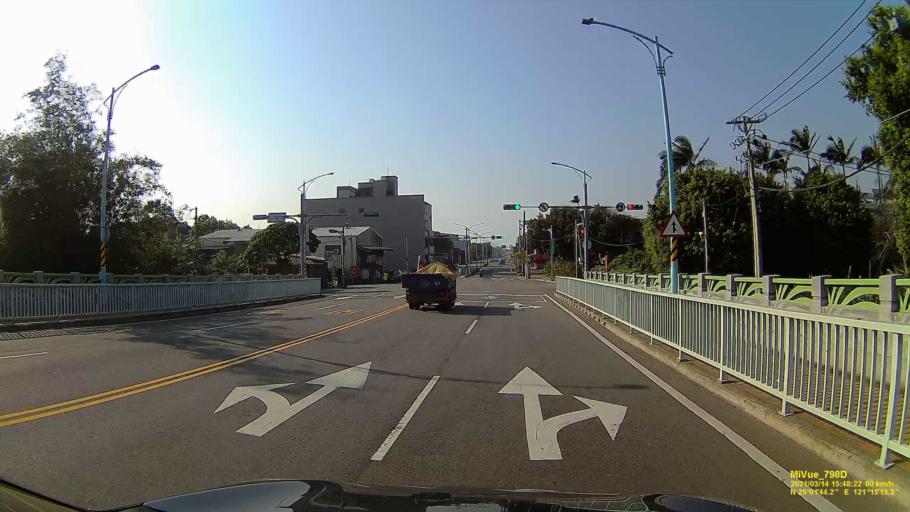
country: TW
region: Taiwan
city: Taoyuan City
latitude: 25.0291
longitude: 121.2535
